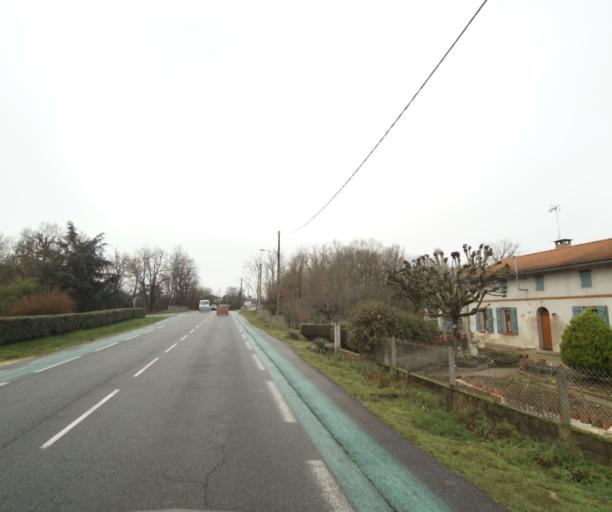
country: FR
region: Midi-Pyrenees
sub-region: Departement de la Haute-Garonne
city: Villemur-sur-Tarn
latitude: 43.8611
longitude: 1.4868
